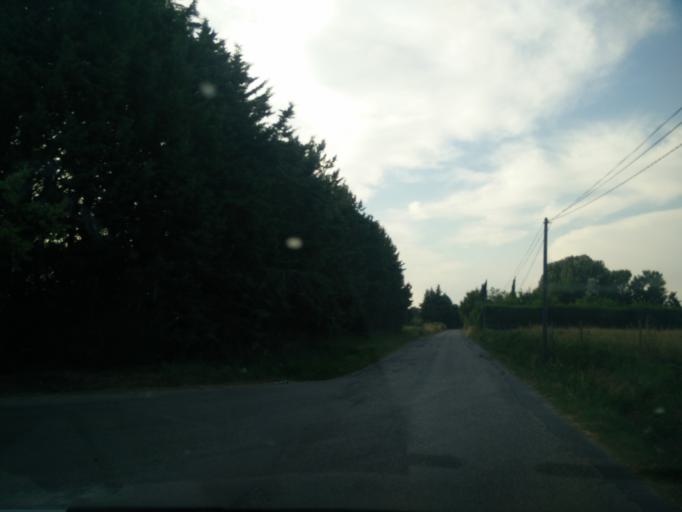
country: FR
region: Languedoc-Roussillon
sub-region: Departement de l'Herault
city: Marsillargues
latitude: 43.6765
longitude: 4.1734
